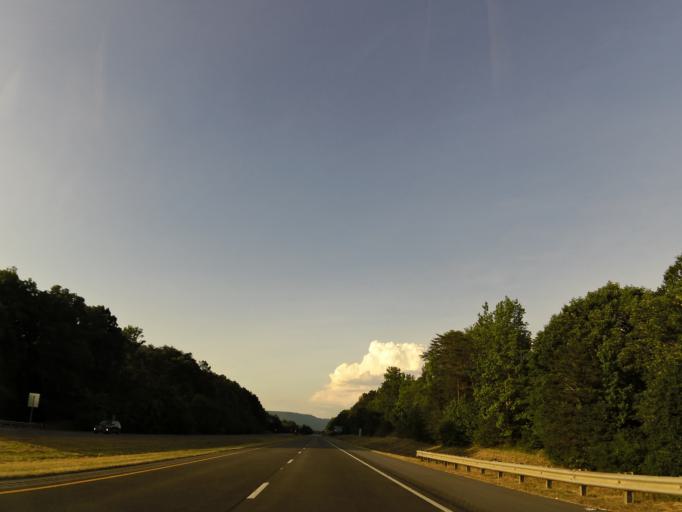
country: US
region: Georgia
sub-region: Dade County
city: Trenton
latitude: 34.7117
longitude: -85.5554
